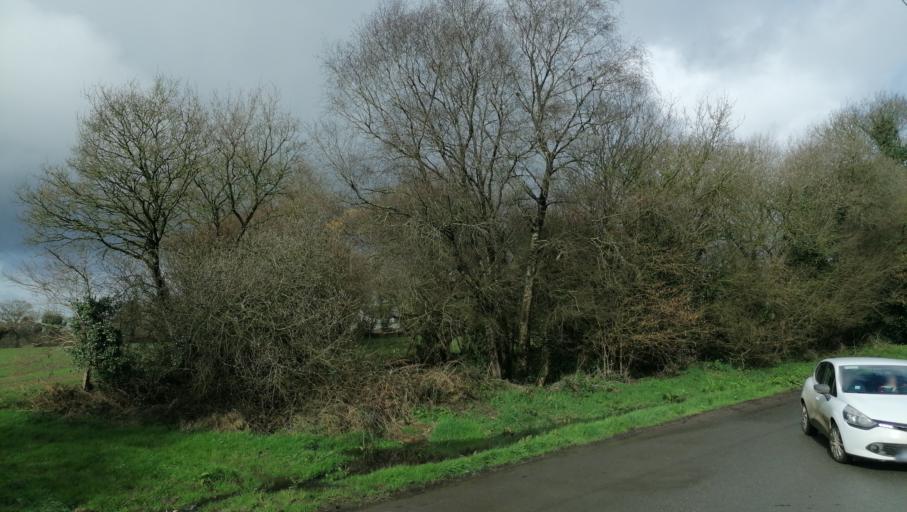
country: FR
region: Brittany
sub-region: Departement des Cotes-d'Armor
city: Lanrodec
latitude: 48.4987
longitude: -3.0265
